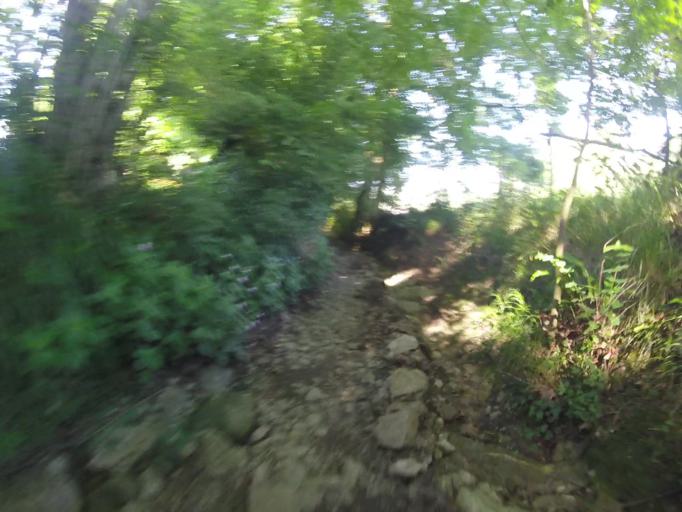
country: ES
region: Basque Country
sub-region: Provincia de Guipuzcoa
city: Pasaia
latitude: 43.3048
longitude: -1.9298
